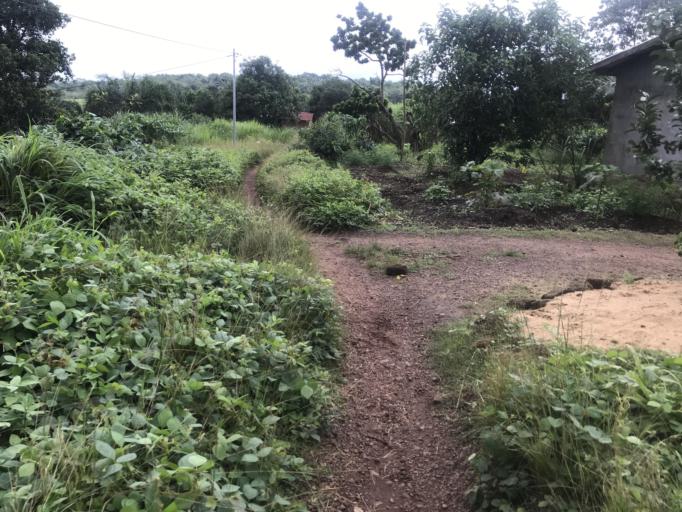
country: SL
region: Eastern Province
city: Buedu
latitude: 8.4609
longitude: -10.3312
